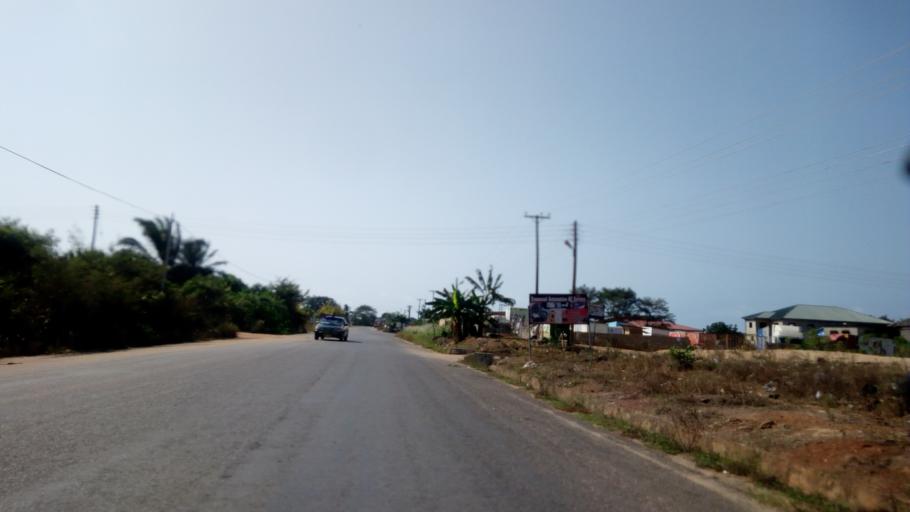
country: GH
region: Central
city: Cape Coast
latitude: 5.1186
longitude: -1.2721
